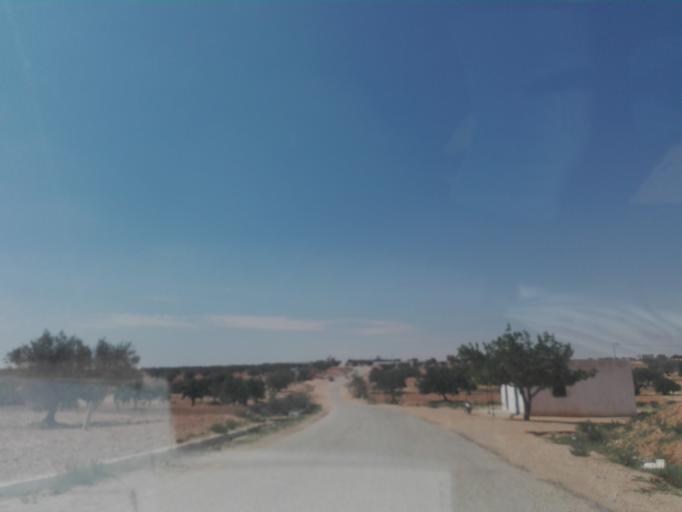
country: TN
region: Safaqis
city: Bi'r `Ali Bin Khalifah
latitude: 34.6178
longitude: 10.3622
